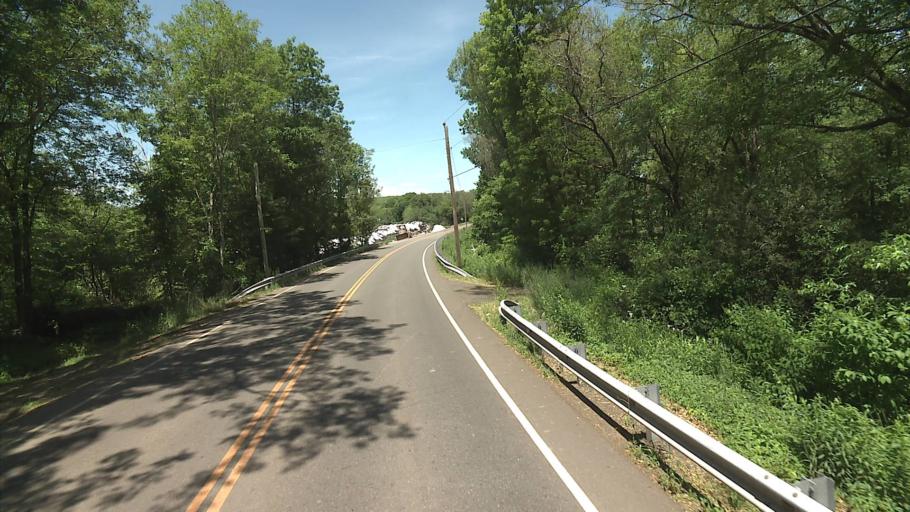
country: US
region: Rhode Island
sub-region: Washington County
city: Hopkinton
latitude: 41.4531
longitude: -71.8127
